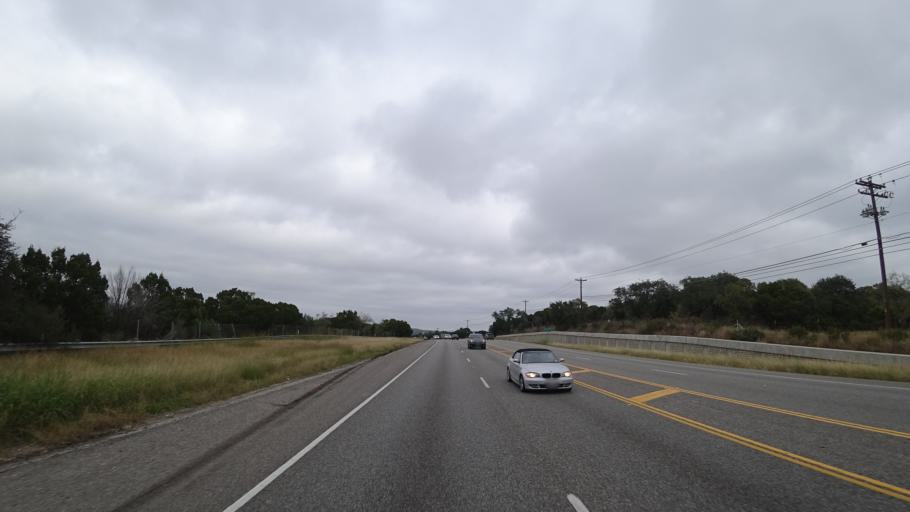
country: US
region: Texas
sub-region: Travis County
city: Bee Cave
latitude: 30.2886
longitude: -97.9174
